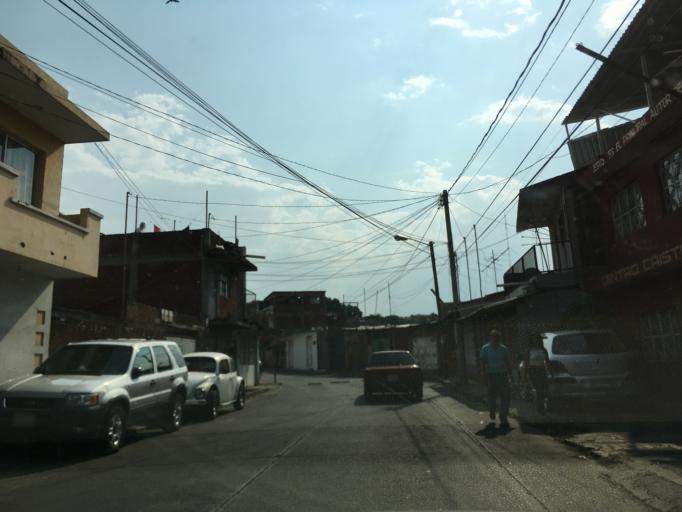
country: MX
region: Michoacan
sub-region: Uruapan
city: Uruapan
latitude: 19.4085
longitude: -102.0629
